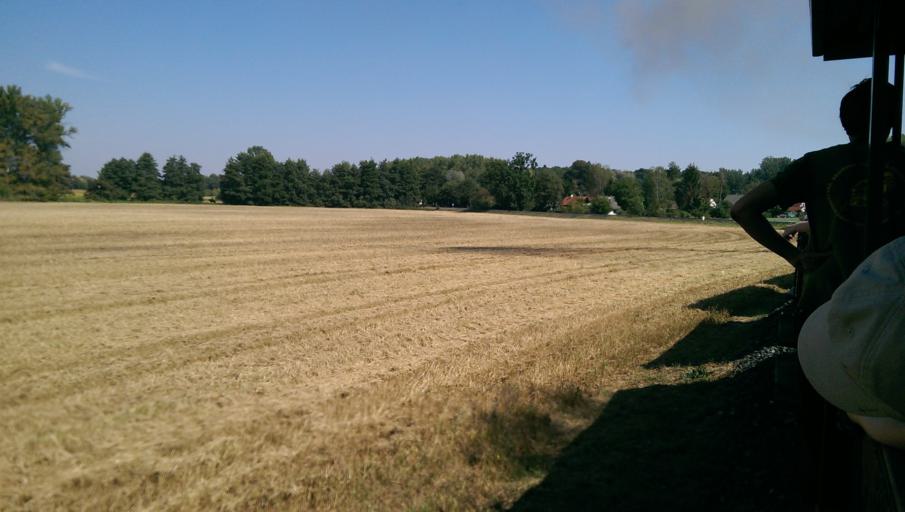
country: CZ
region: Central Bohemia
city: Stary Kolin
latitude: 50.0551
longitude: 15.2634
